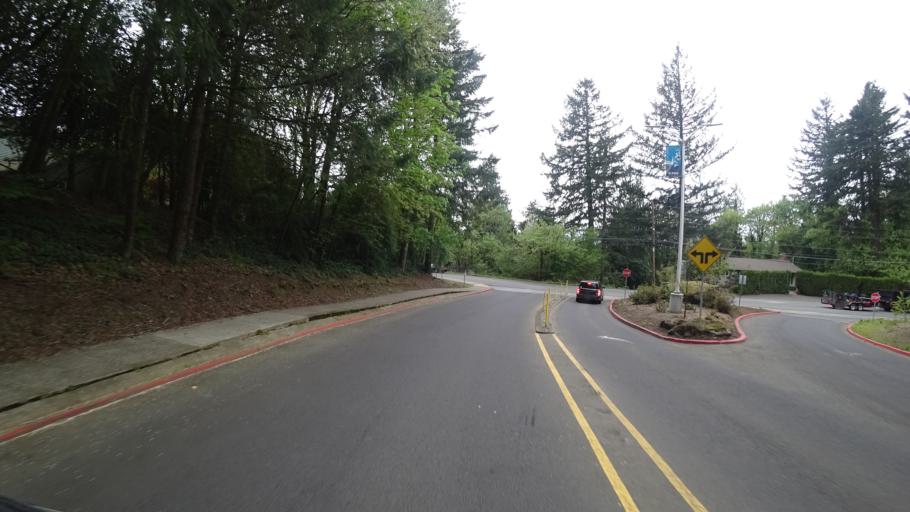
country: US
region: Oregon
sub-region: Washington County
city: Metzger
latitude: 45.4405
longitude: -122.7378
